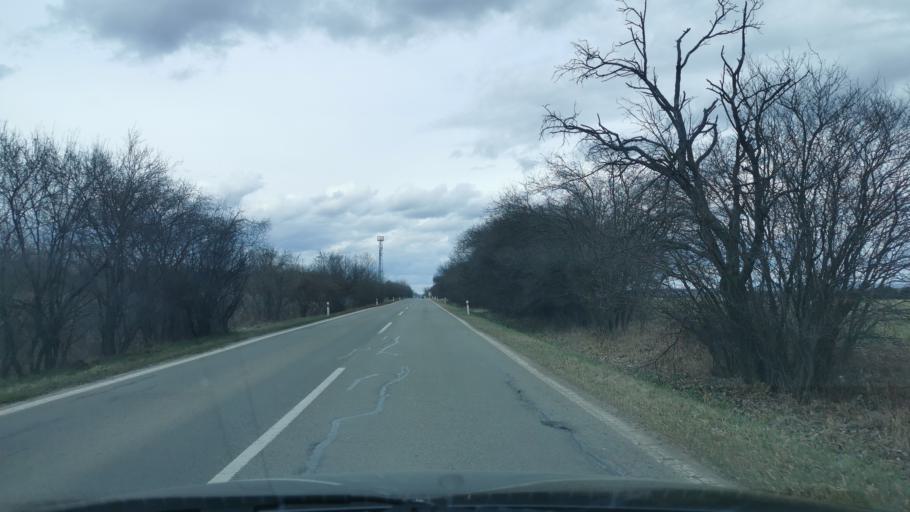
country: SK
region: Trnavsky
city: Gbely
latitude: 48.7757
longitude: 17.1003
